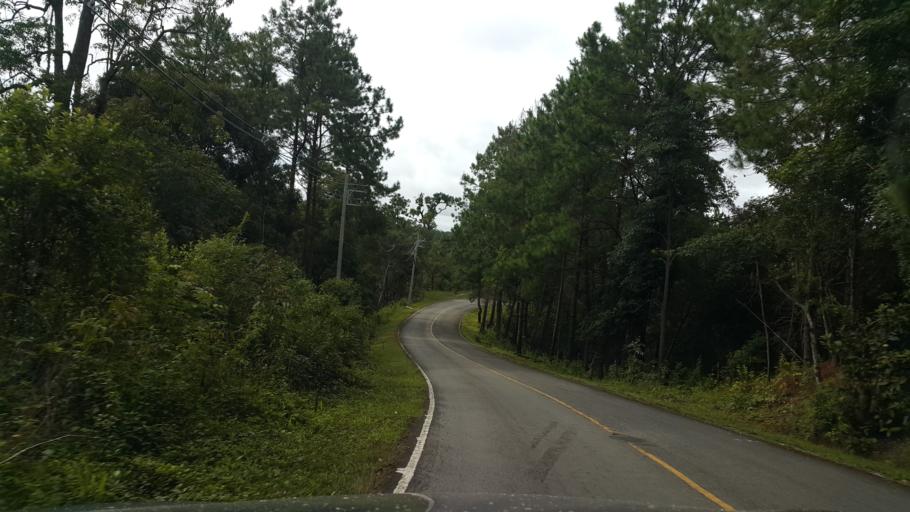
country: TH
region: Chiang Mai
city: Samoeng
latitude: 18.8950
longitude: 98.4987
